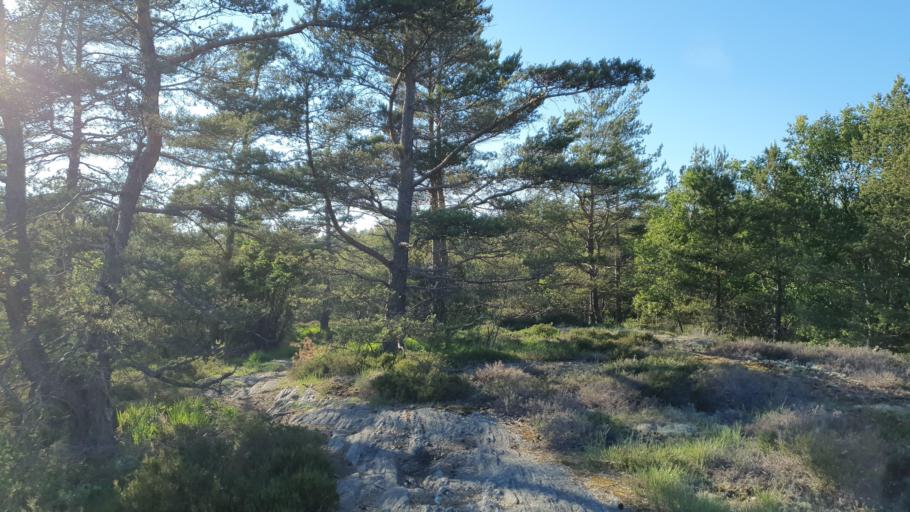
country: SE
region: Vaestra Goetaland
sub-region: Molndal
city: Kallered
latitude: 57.6308
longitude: 12.0619
